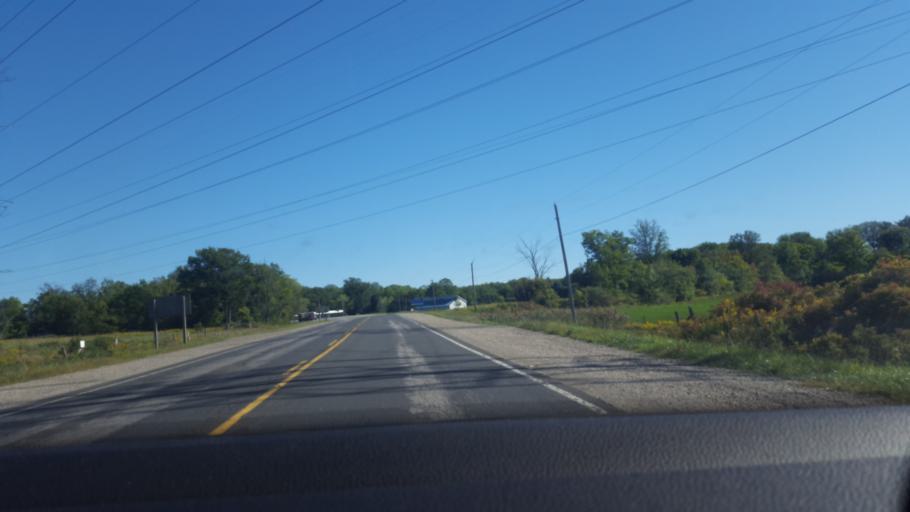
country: CA
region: Ontario
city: Hamilton
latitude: 43.1503
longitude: -79.7157
